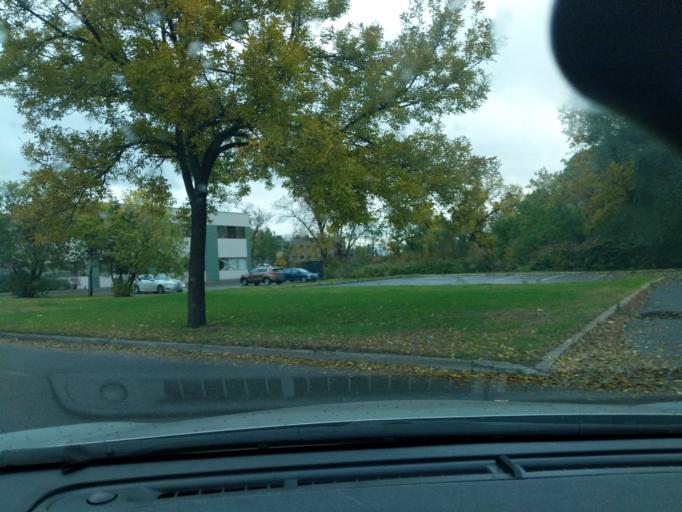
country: CA
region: Quebec
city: L'Ancienne-Lorette
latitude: 46.8030
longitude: -71.3249
